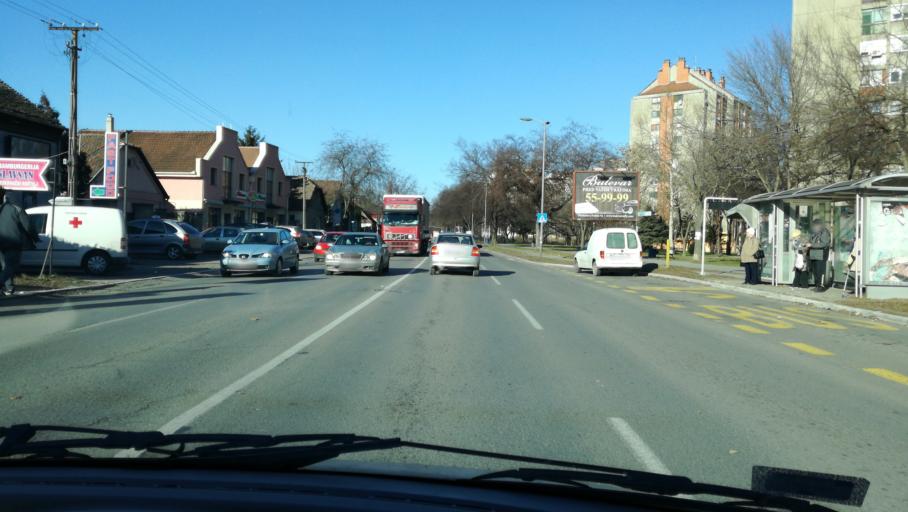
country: RS
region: Autonomna Pokrajina Vojvodina
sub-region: Severnobacki Okrug
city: Subotica
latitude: 46.0843
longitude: 19.6722
